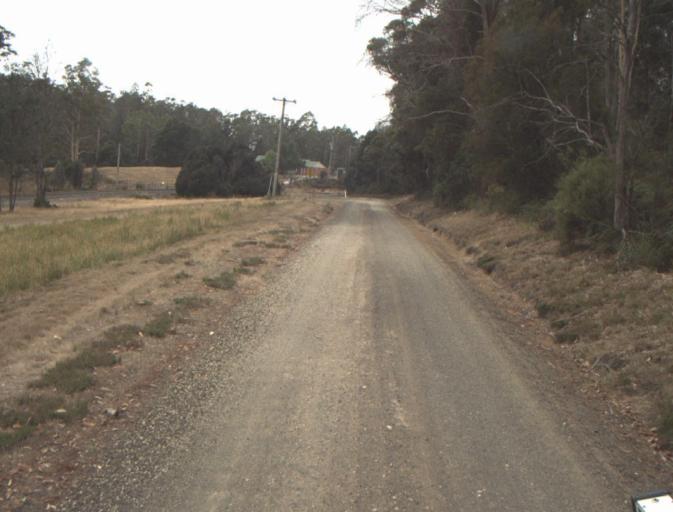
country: AU
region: Tasmania
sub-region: Dorset
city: Bridport
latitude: -41.1770
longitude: 147.2642
